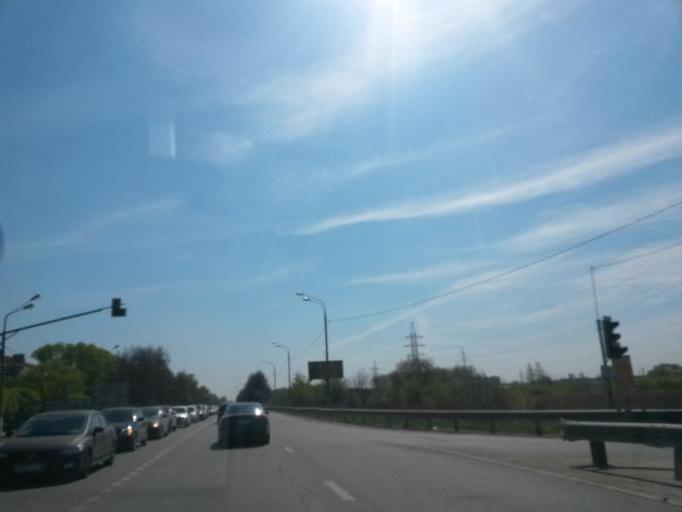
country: RU
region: Moskovskaya
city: Klimovsk
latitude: 55.3807
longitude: 37.5358
